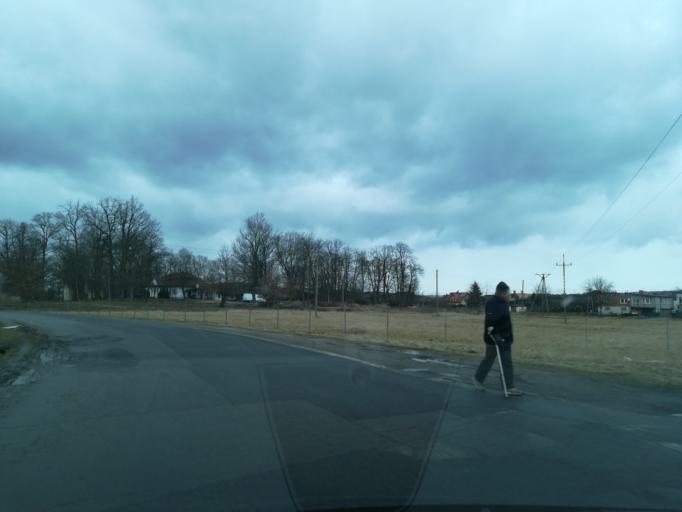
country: PL
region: Lesser Poland Voivodeship
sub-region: Krakow
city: Sidzina
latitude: 49.9884
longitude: 19.8715
